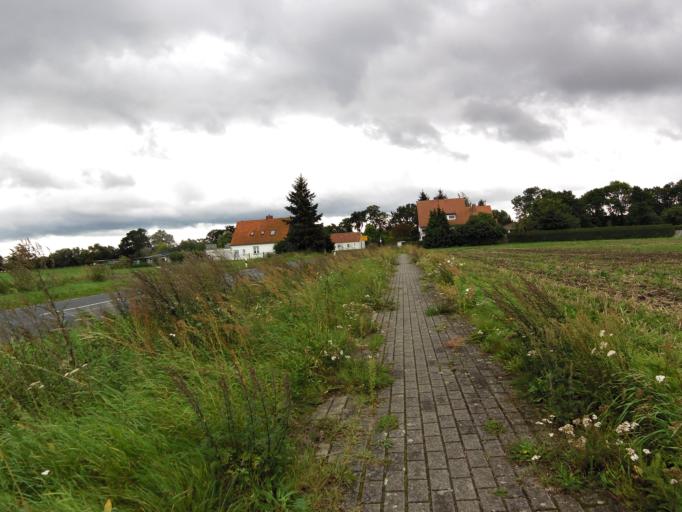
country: DE
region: Saxony-Anhalt
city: Hohenberg-Krusemark
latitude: 52.7078
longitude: 11.9594
